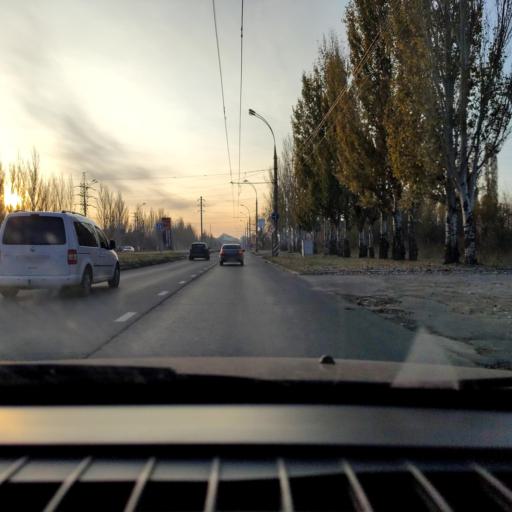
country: RU
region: Samara
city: Tol'yatti
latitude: 53.5473
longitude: 49.2741
